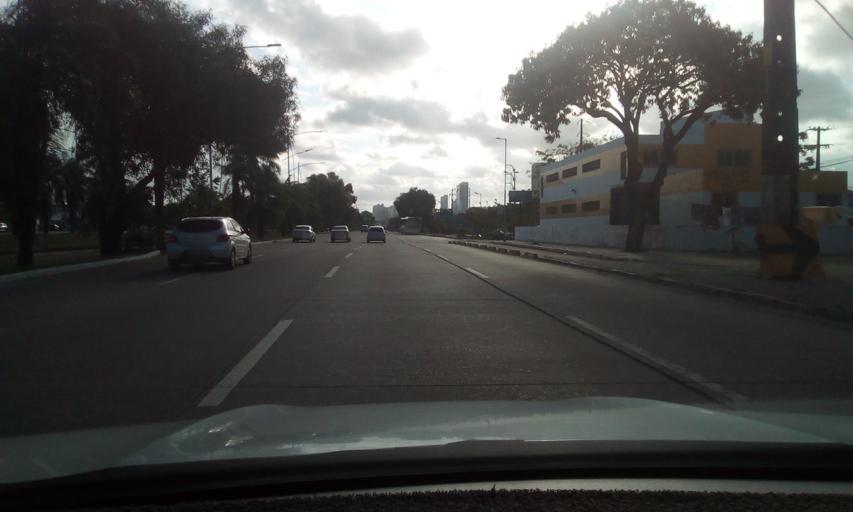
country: BR
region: Pernambuco
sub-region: Recife
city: Recife
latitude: -8.0372
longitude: -34.8739
